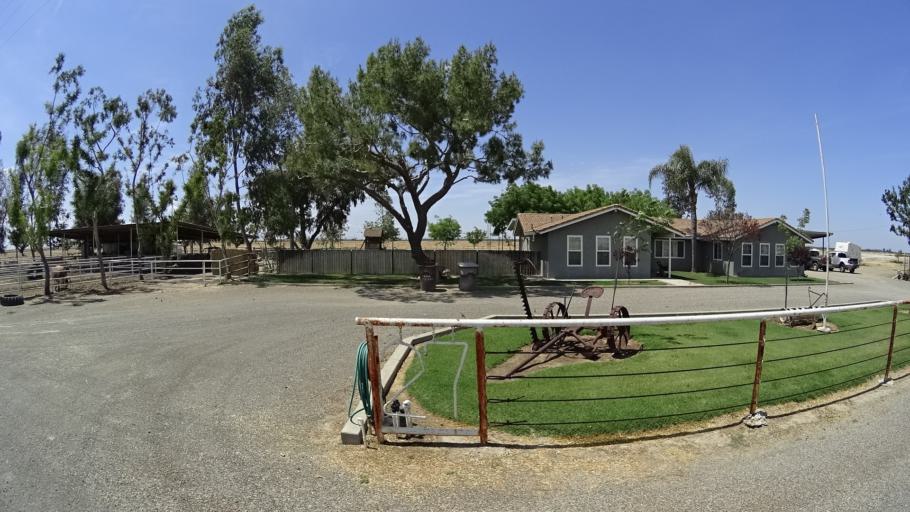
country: US
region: California
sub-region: Kings County
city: Home Garden
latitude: 36.2285
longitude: -119.6729
